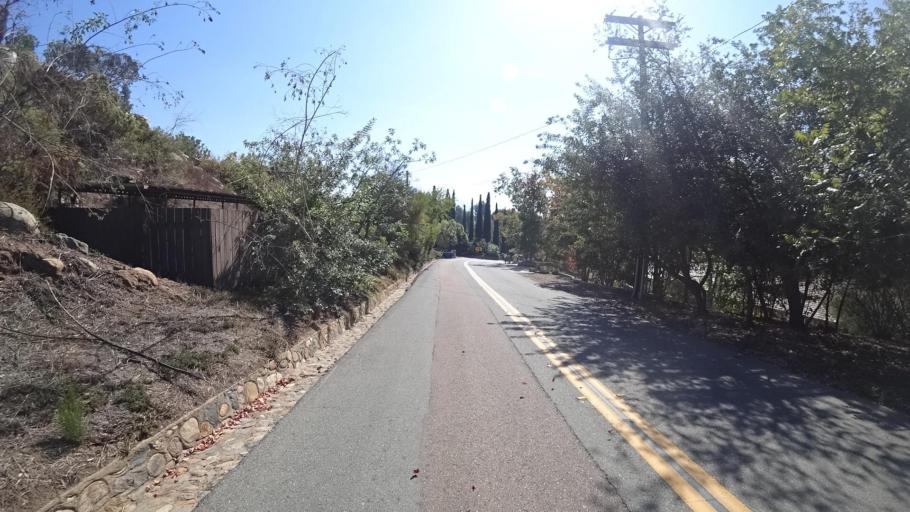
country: US
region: California
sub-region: San Diego County
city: Bostonia
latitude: 32.7777
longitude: -116.9345
